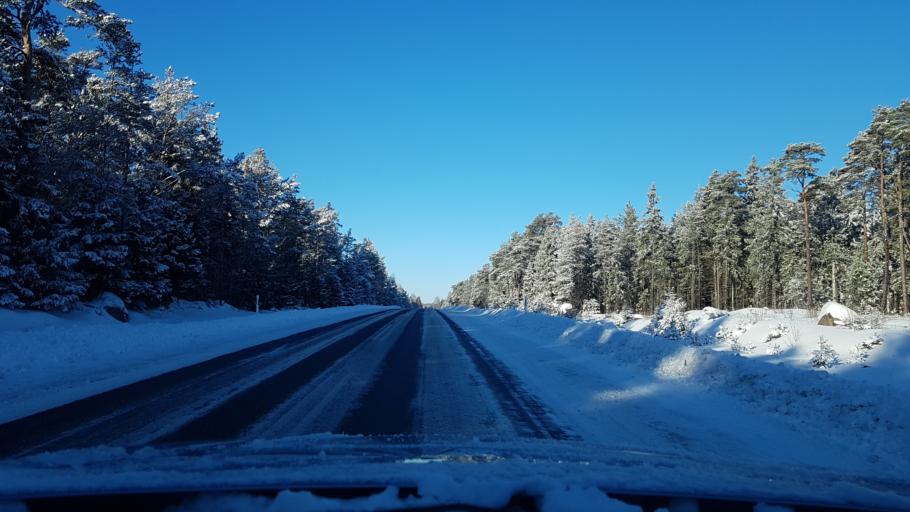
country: EE
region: Hiiumaa
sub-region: Kaerdla linn
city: Kardla
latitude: 58.9594
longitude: 22.8545
